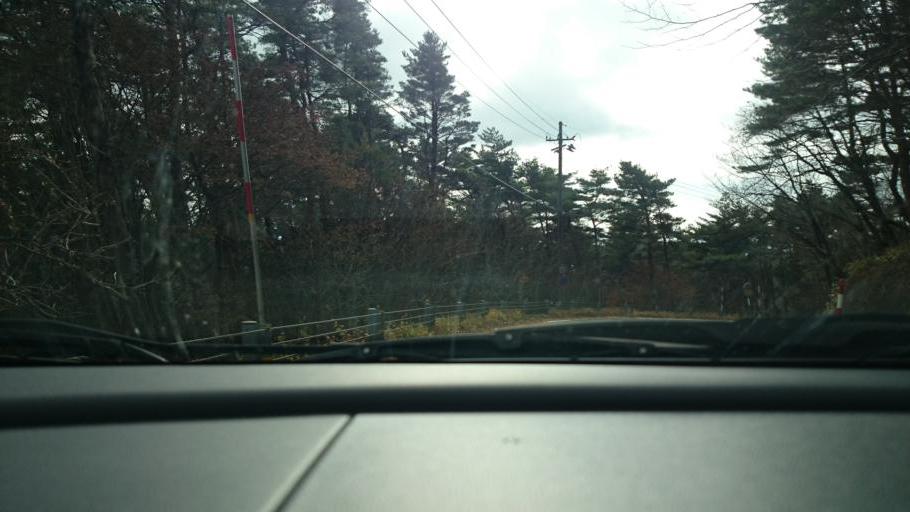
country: JP
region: Tochigi
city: Kuroiso
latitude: 37.1669
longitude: 140.0297
